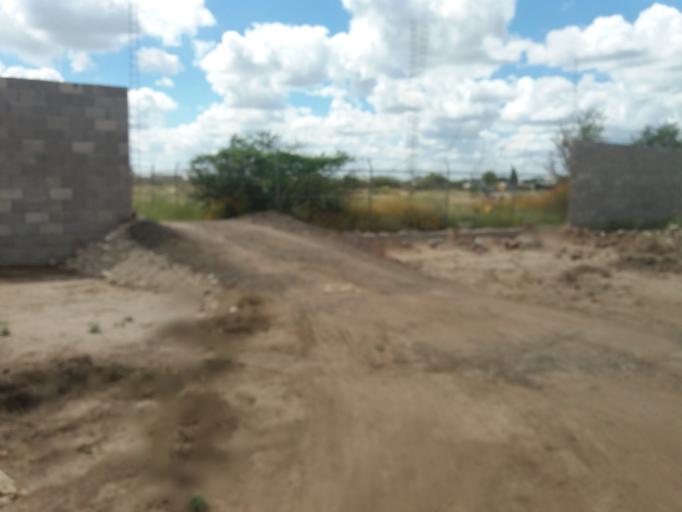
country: MX
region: Aguascalientes
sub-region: Aguascalientes
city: San Sebastian [Fraccionamiento]
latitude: 21.8219
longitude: -102.2727
